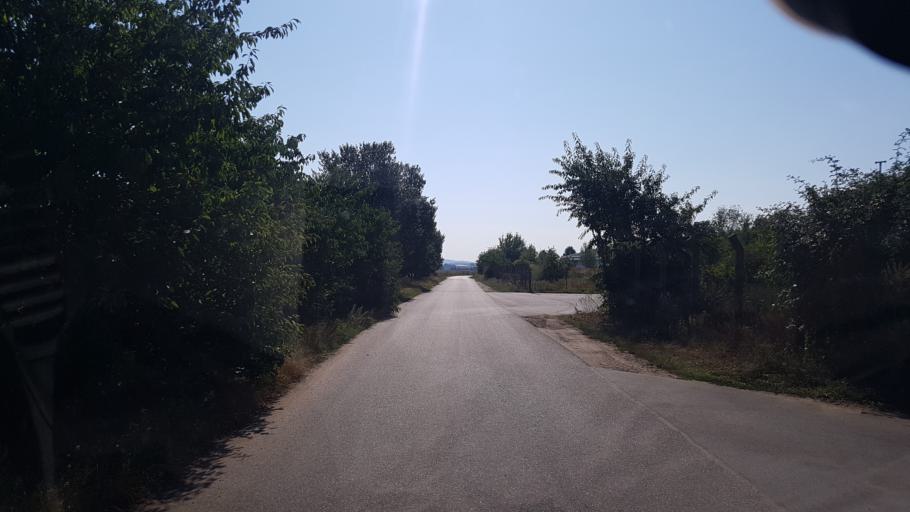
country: DE
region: Brandenburg
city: Groden
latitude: 51.4047
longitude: 13.5865
